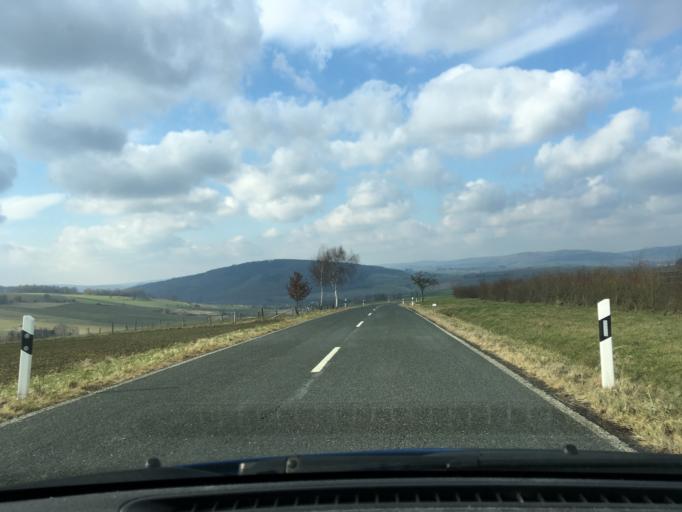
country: DE
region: Lower Saxony
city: Uslar
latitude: 51.6087
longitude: 9.6323
